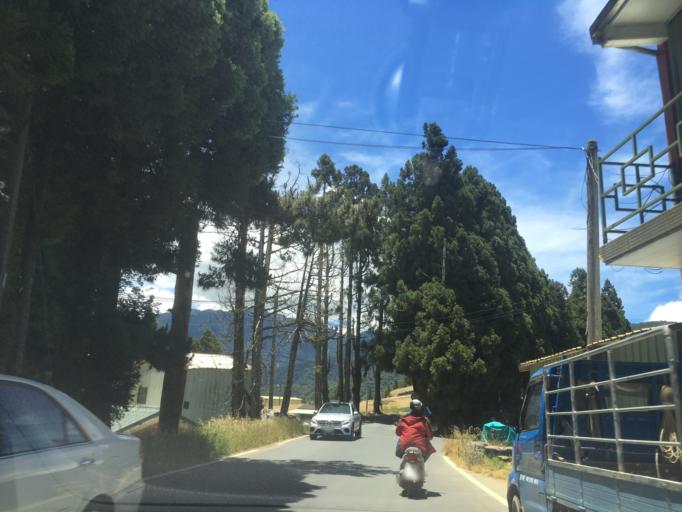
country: TW
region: Taiwan
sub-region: Nantou
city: Puli
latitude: 24.2430
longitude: 121.2463
